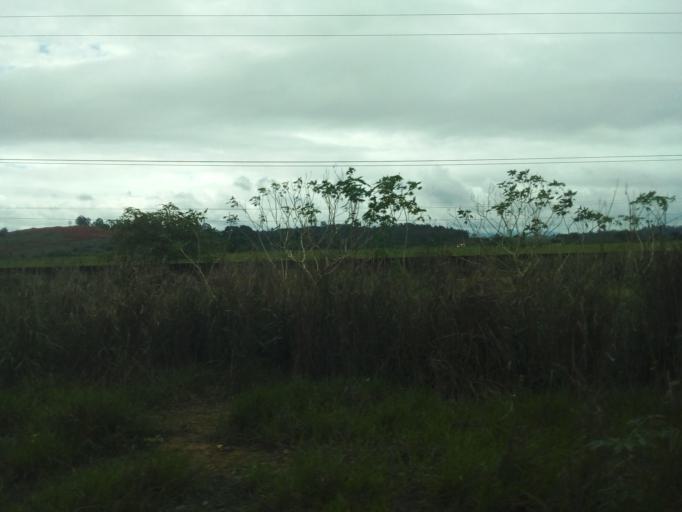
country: BR
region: Minas Gerais
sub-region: Ipatinga
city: Ipatinga
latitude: -19.4666
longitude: -42.4777
